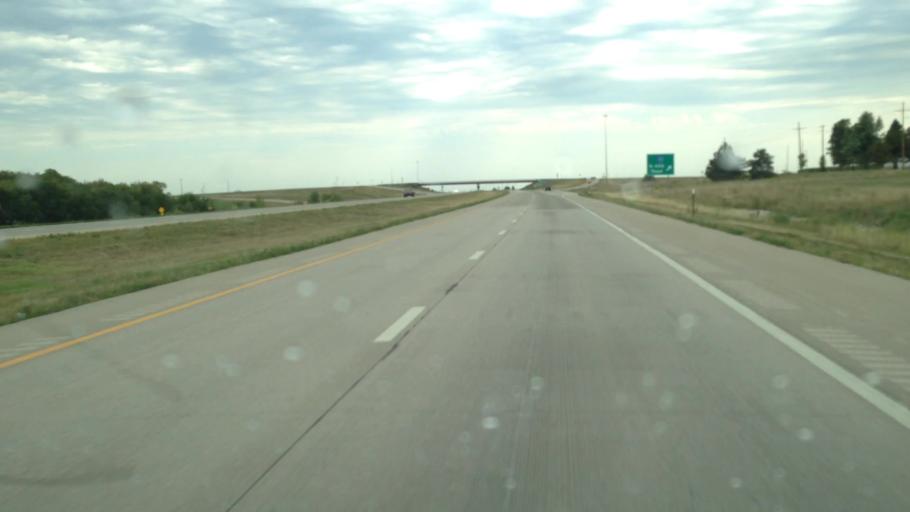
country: US
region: Kansas
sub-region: Douglas County
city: Baldwin City
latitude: 38.8394
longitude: -95.2686
